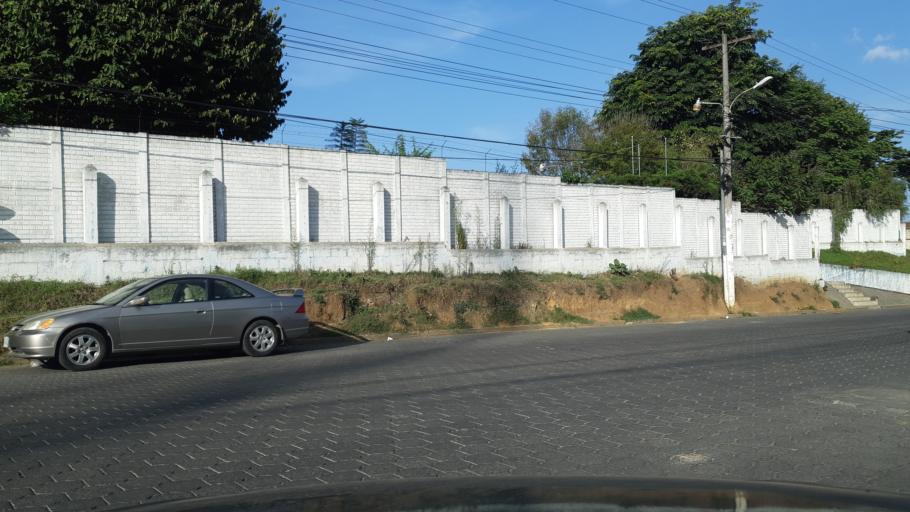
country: GT
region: Chimaltenango
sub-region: Municipio de Chimaltenango
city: Chimaltenango
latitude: 14.6612
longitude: -90.8298
